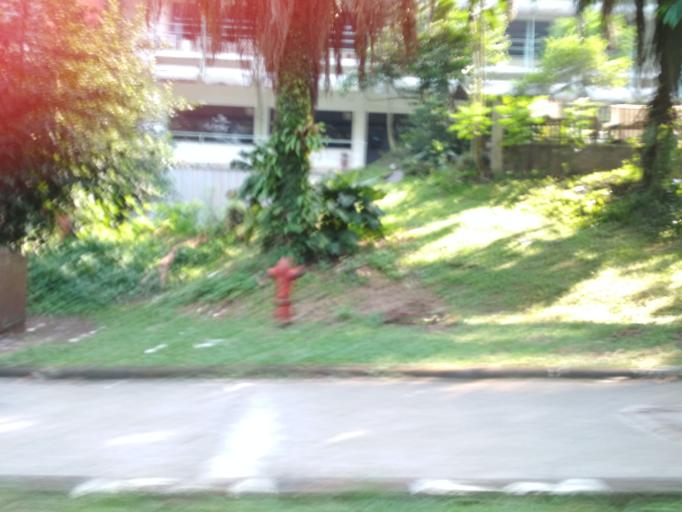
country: ID
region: West Java
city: Ciampea
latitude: -6.5598
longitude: 106.7292
